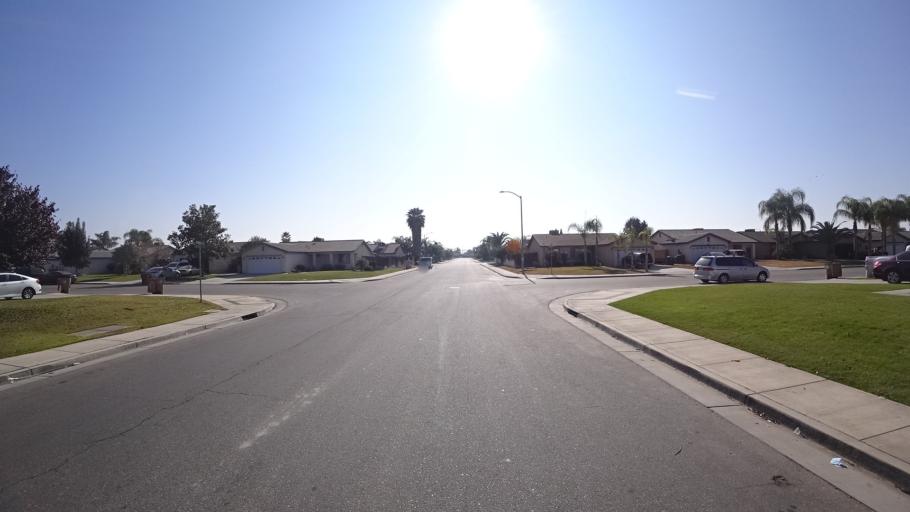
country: US
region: California
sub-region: Kern County
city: Greenfield
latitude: 35.2810
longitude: -119.0174
